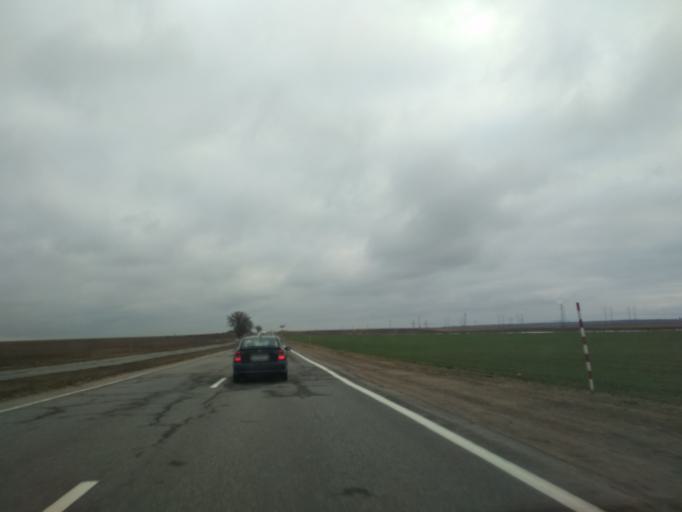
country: BY
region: Minsk
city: Dukora
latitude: 53.6917
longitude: 27.9015
